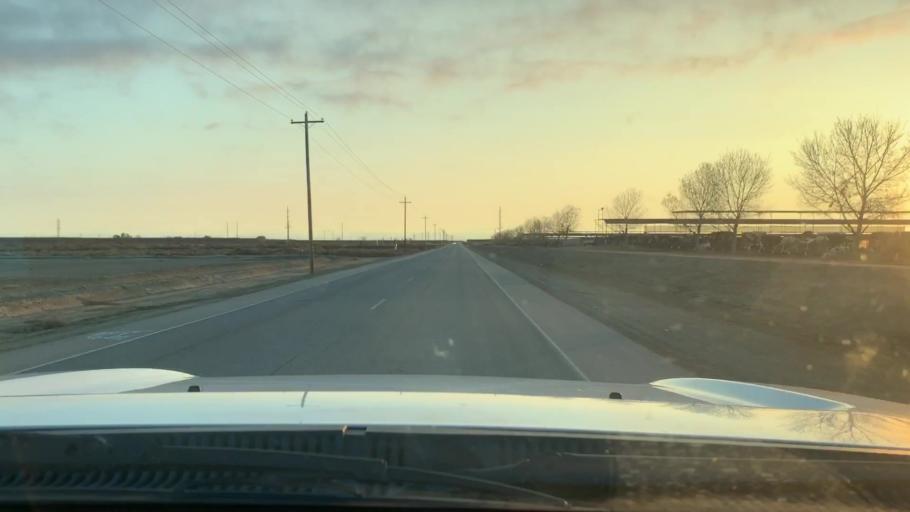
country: US
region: California
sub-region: Kern County
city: Buttonwillow
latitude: 35.5005
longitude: -119.4555
